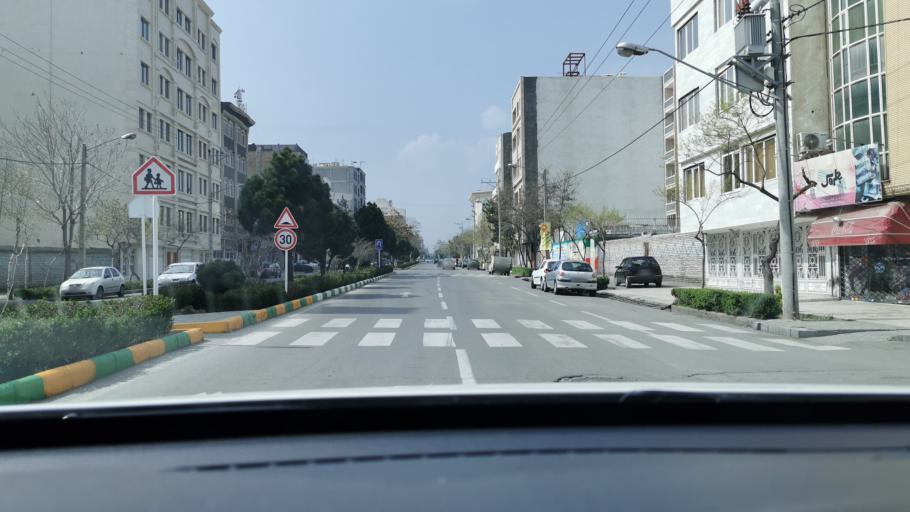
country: IR
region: Razavi Khorasan
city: Mashhad
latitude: 36.3275
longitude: 59.5166
